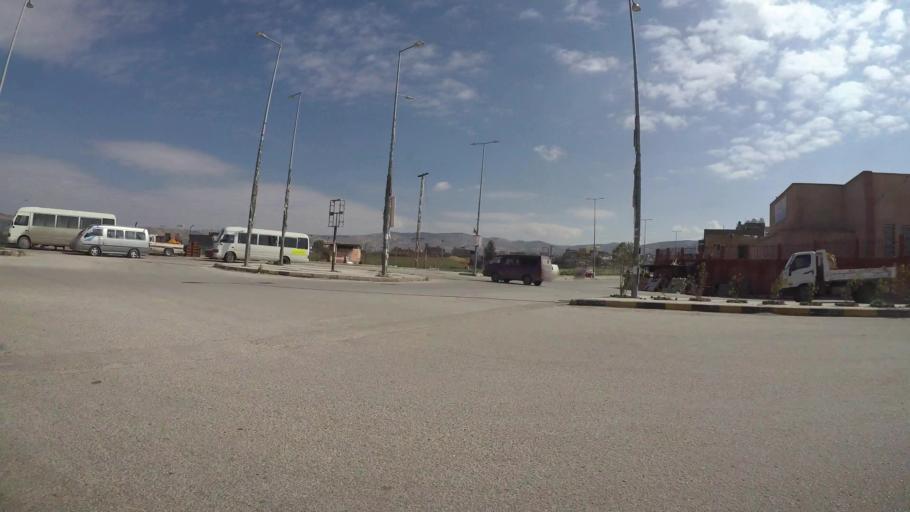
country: JO
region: Amman
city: Al Jubayhah
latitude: 32.0805
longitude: 35.8456
